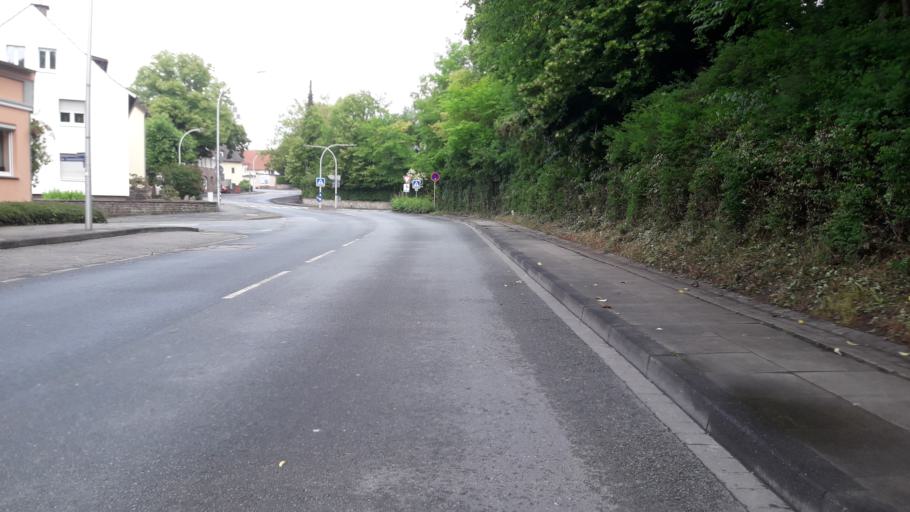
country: DE
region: North Rhine-Westphalia
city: Warburg
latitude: 51.4930
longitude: 9.1606
